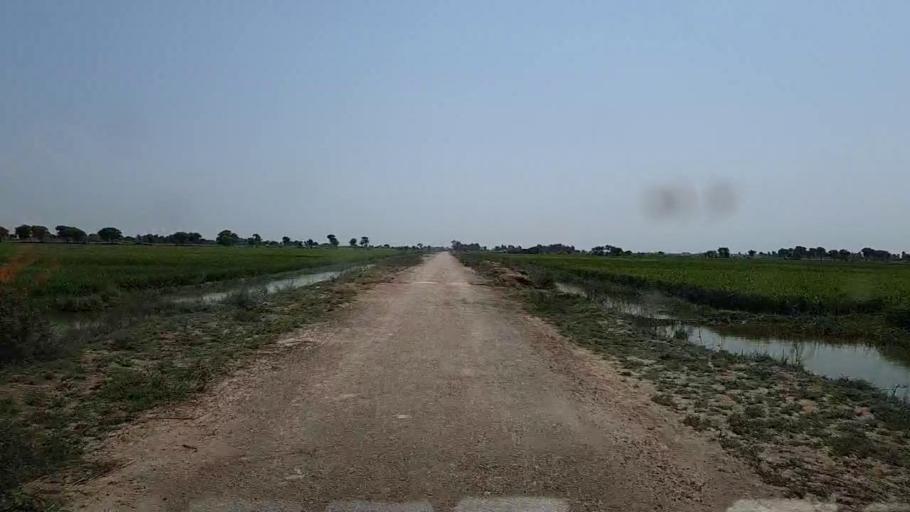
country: PK
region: Sindh
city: Mirpur Batoro
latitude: 24.6084
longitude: 68.4523
